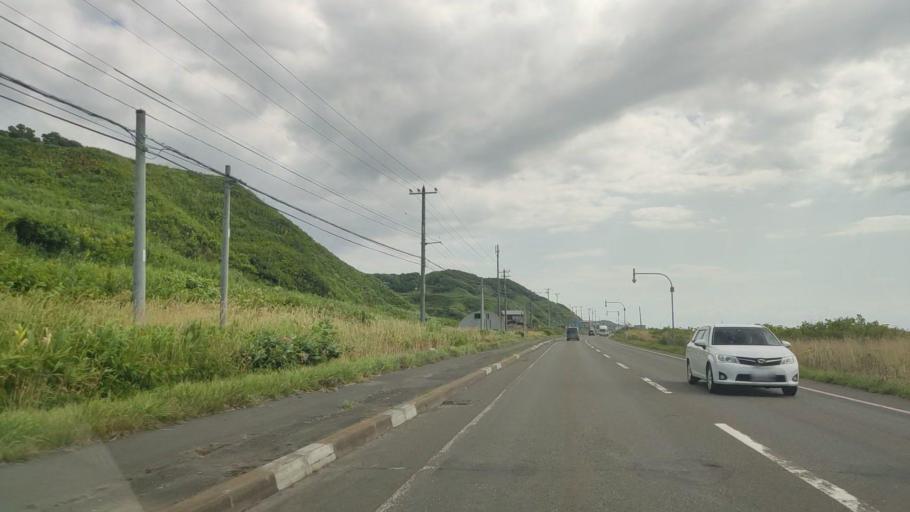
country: JP
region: Hokkaido
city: Rumoi
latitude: 44.1837
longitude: 141.6588
